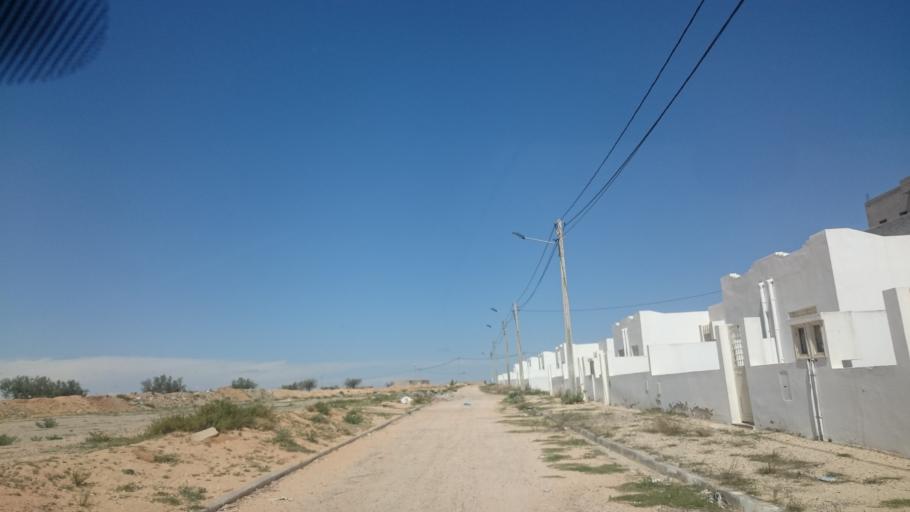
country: TN
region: Safaqis
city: Sfax
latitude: 34.7475
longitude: 10.5128
